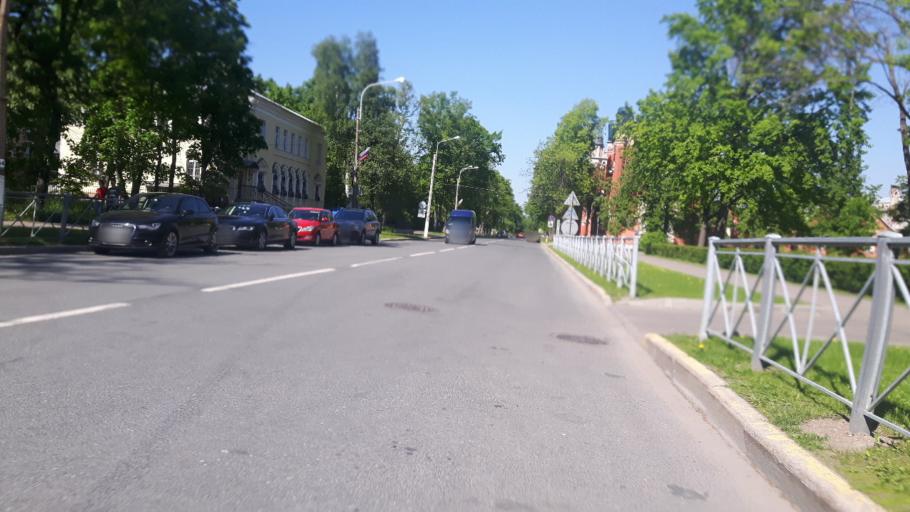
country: RU
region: St.-Petersburg
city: Peterhof
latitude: 59.8783
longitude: 29.9235
